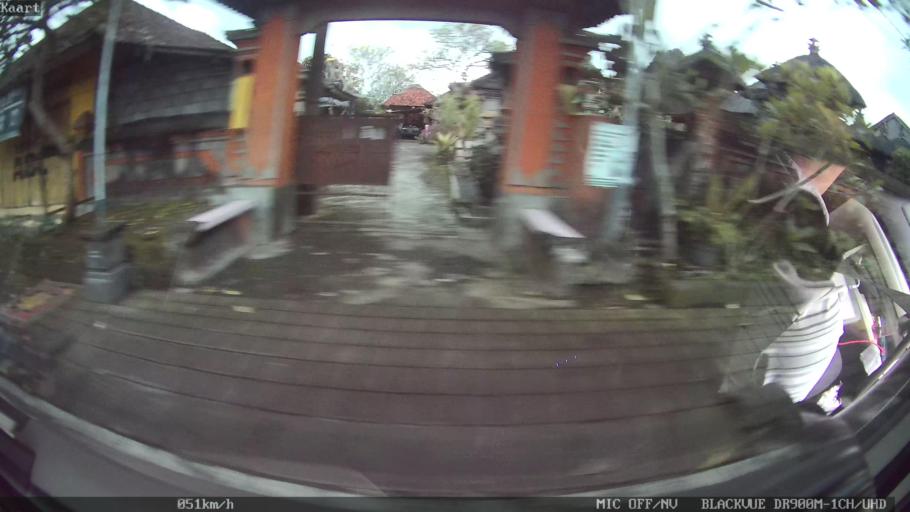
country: ID
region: Bali
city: Petang
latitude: -8.3992
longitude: 115.2186
